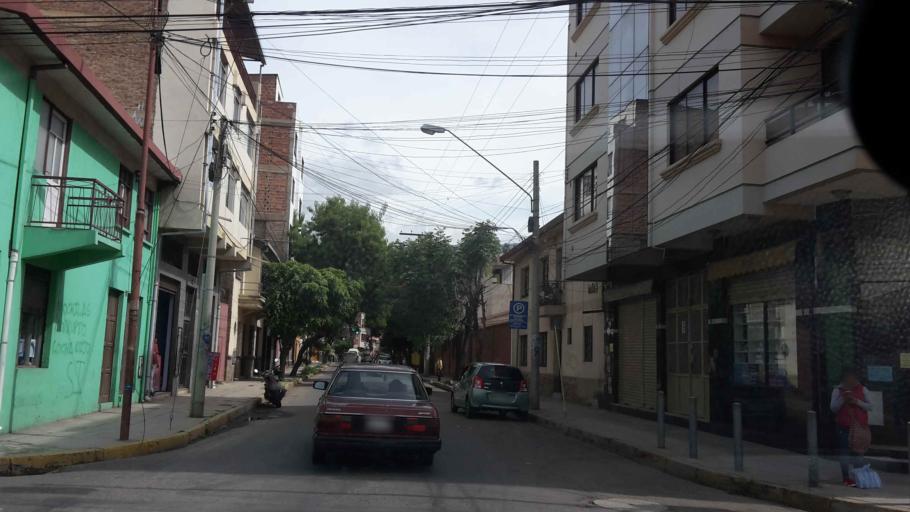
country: BO
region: Cochabamba
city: Cochabamba
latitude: -17.3958
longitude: -66.1645
